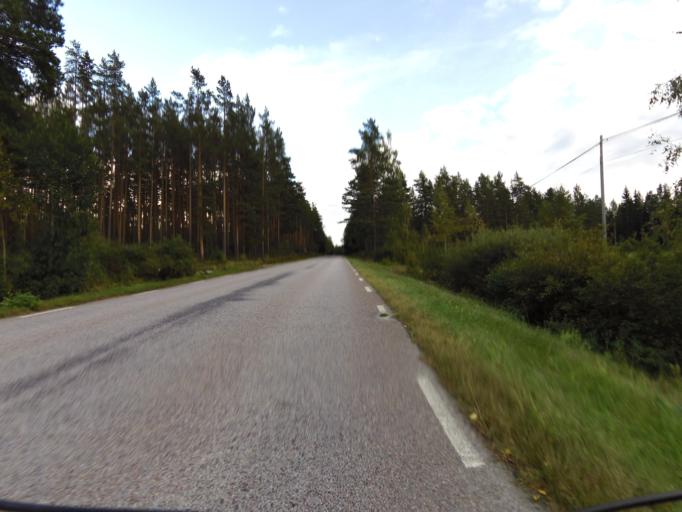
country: SE
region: Gaevleborg
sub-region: Gavle Kommun
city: Valbo
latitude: 60.6626
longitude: 16.9632
